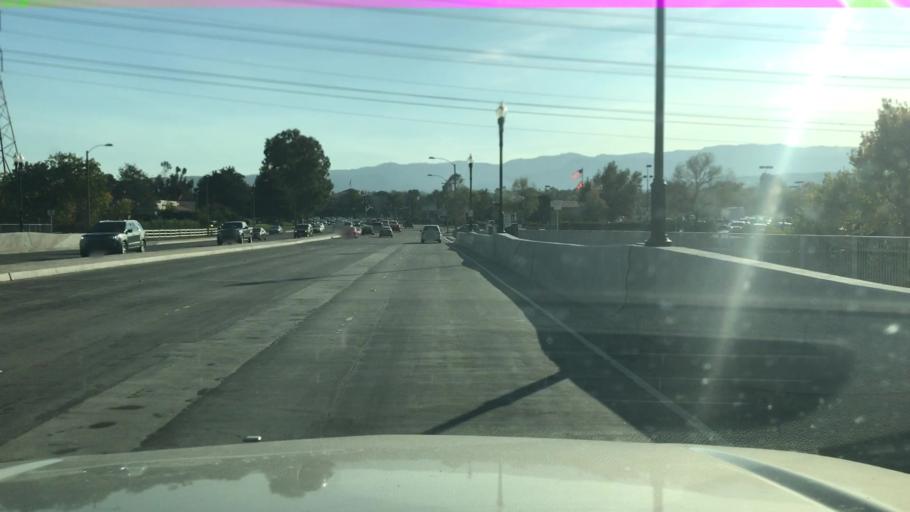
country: US
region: California
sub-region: Los Angeles County
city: Santa Clarita
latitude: 34.4243
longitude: -118.5623
